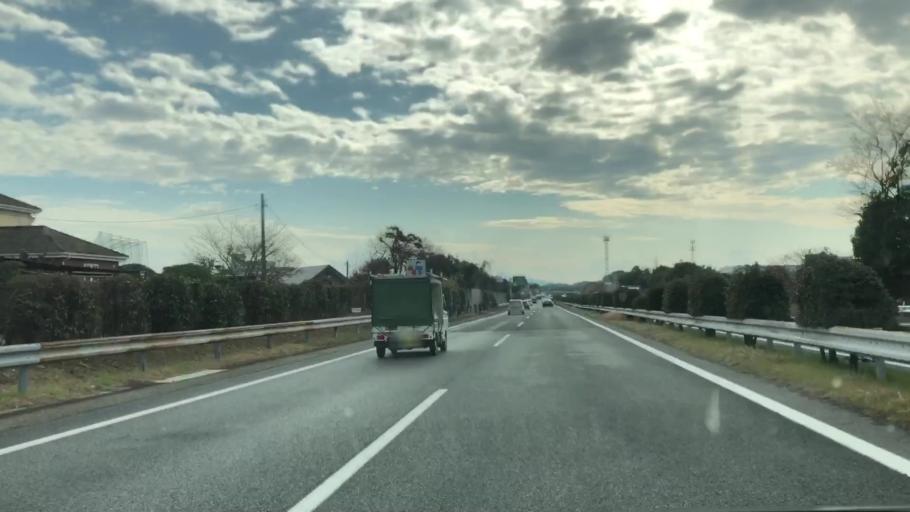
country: JP
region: Fukuoka
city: Kurume
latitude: 33.2637
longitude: 130.5386
